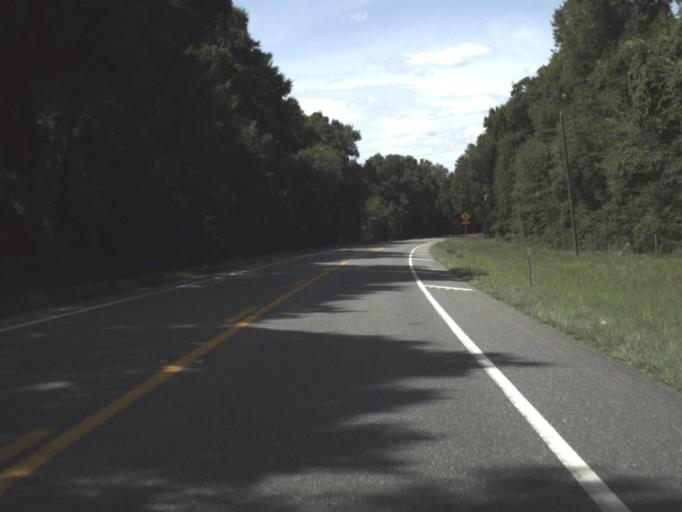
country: US
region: Florida
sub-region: Alachua County
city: High Springs
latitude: 29.8604
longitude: -82.7418
